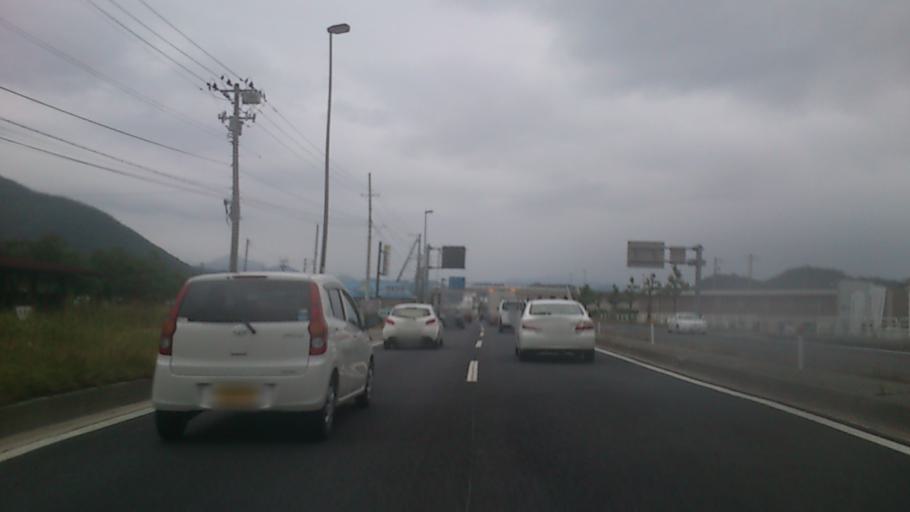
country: JP
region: Yamagata
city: Tendo
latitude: 38.3734
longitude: 140.3832
